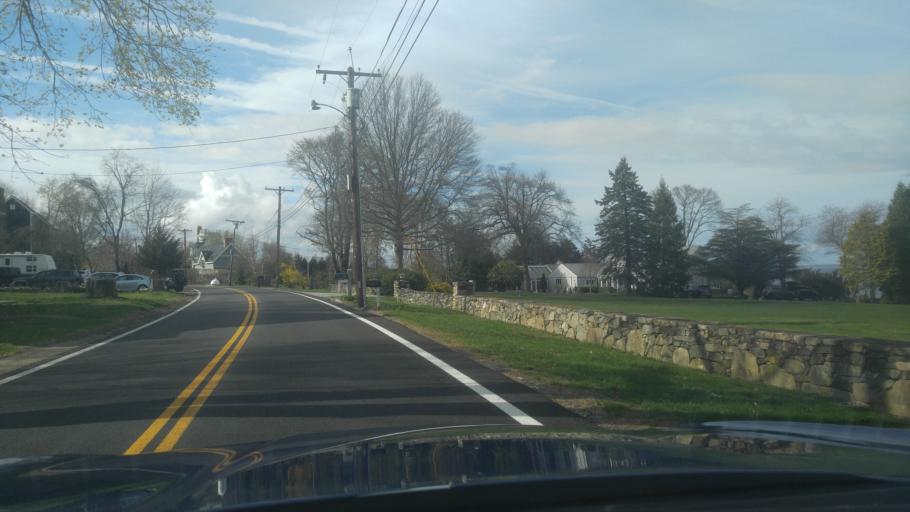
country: US
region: Rhode Island
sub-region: Newport County
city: Jamestown
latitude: 41.5690
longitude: -71.3651
